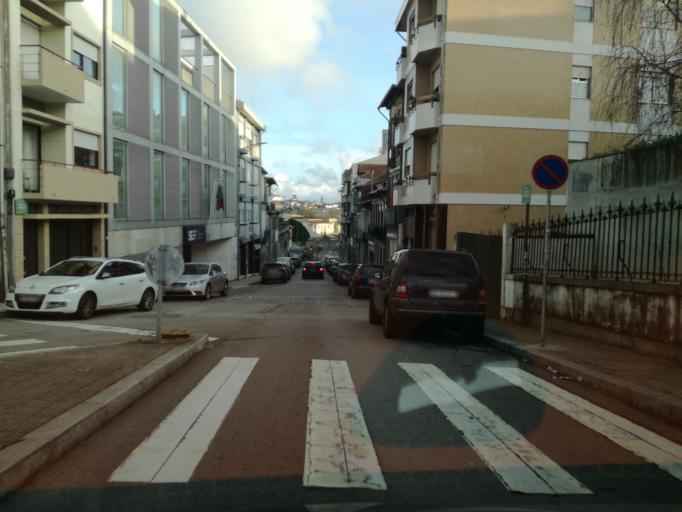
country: PT
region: Porto
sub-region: Porto
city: Porto
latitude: 41.1601
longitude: -8.6212
